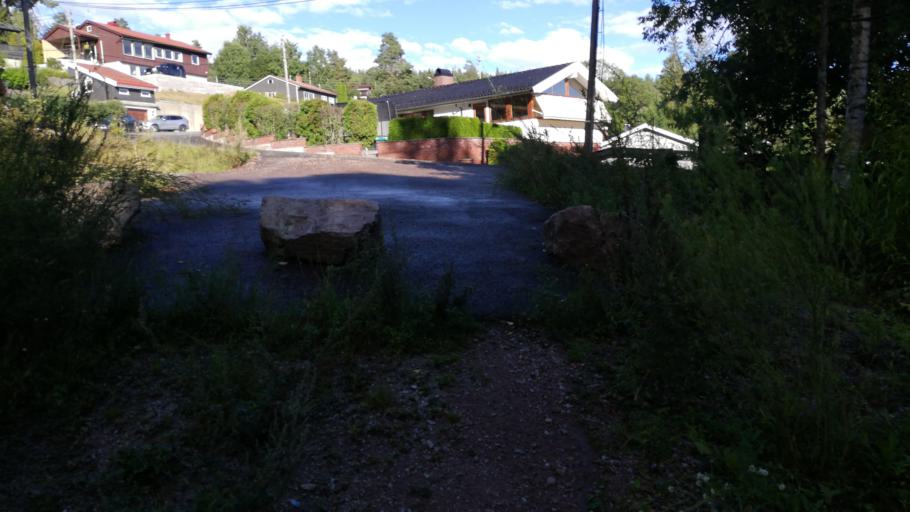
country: NO
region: Buskerud
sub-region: Drammen
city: Drammen
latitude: 59.7588
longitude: 10.1741
